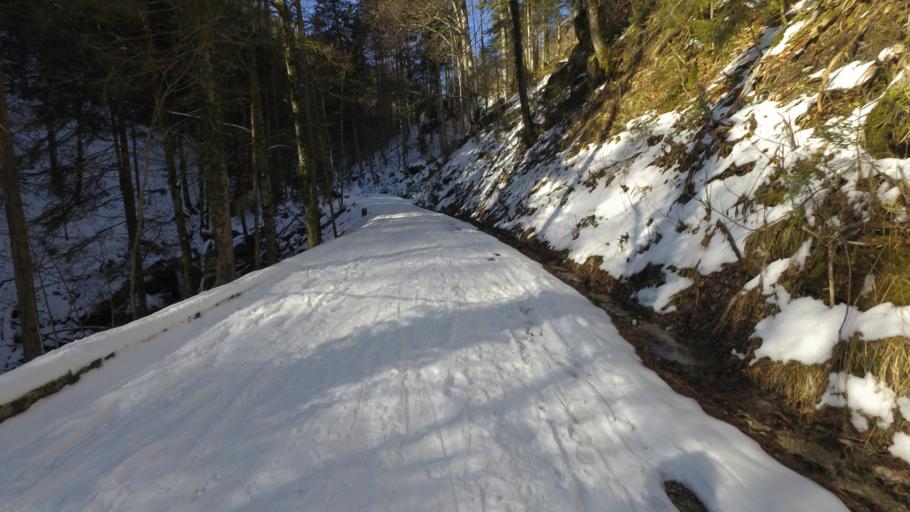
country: DE
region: Bavaria
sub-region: Upper Bavaria
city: Ruhpolding
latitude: 47.7488
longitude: 12.6048
